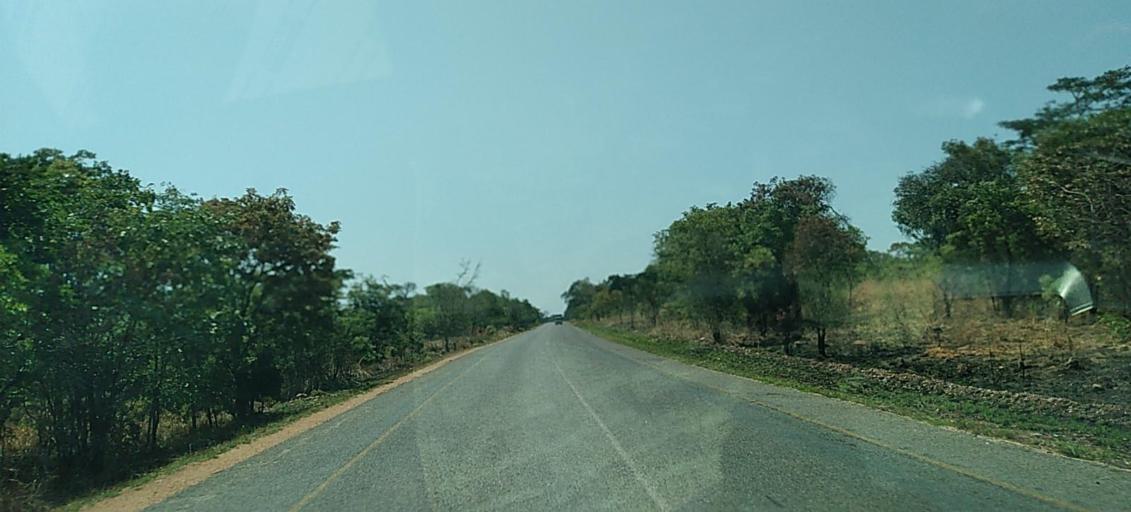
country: ZM
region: North-Western
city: Solwezi
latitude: -12.2873
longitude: 25.7888
